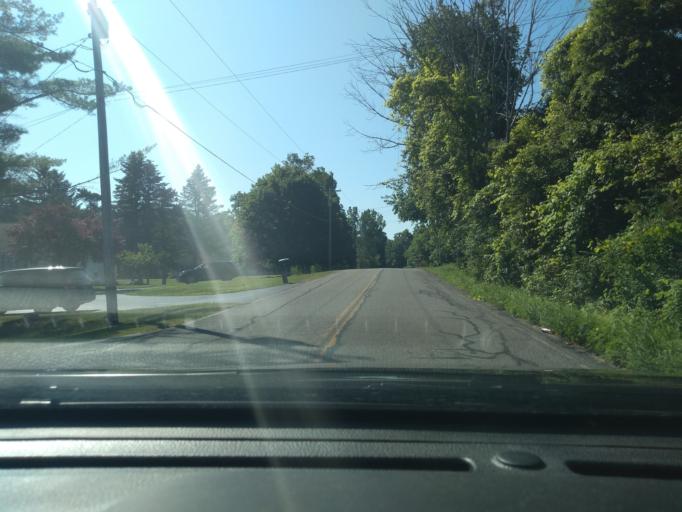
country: US
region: New York
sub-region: Erie County
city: Orchard Park
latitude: 42.7851
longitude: -78.6869
